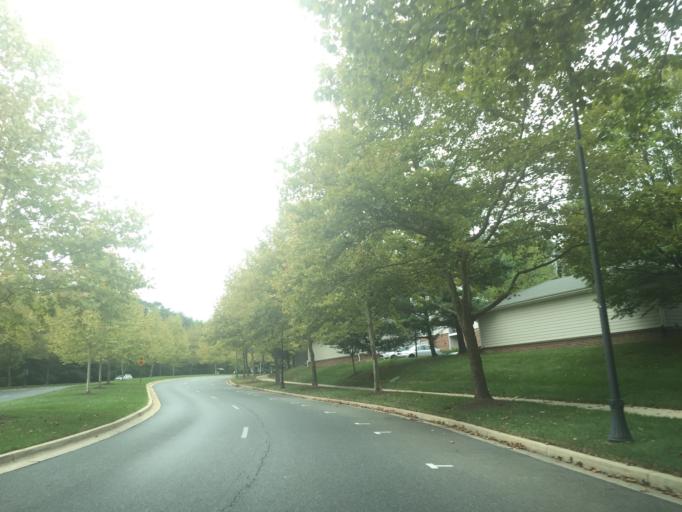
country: US
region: Maryland
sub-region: Montgomery County
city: Gaithersburg
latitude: 39.1245
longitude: -77.2410
